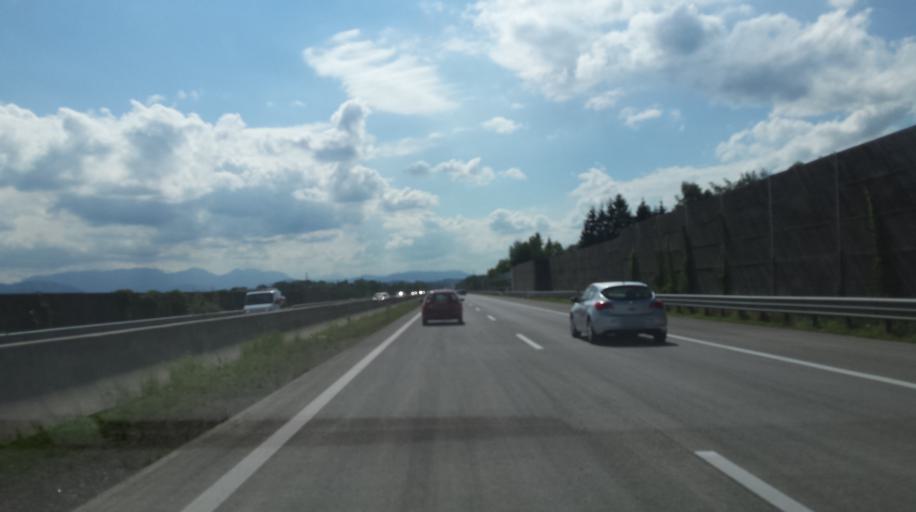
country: AT
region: Upper Austria
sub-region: Politischer Bezirk Gmunden
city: Vorchdorf
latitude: 48.0220
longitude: 13.9591
